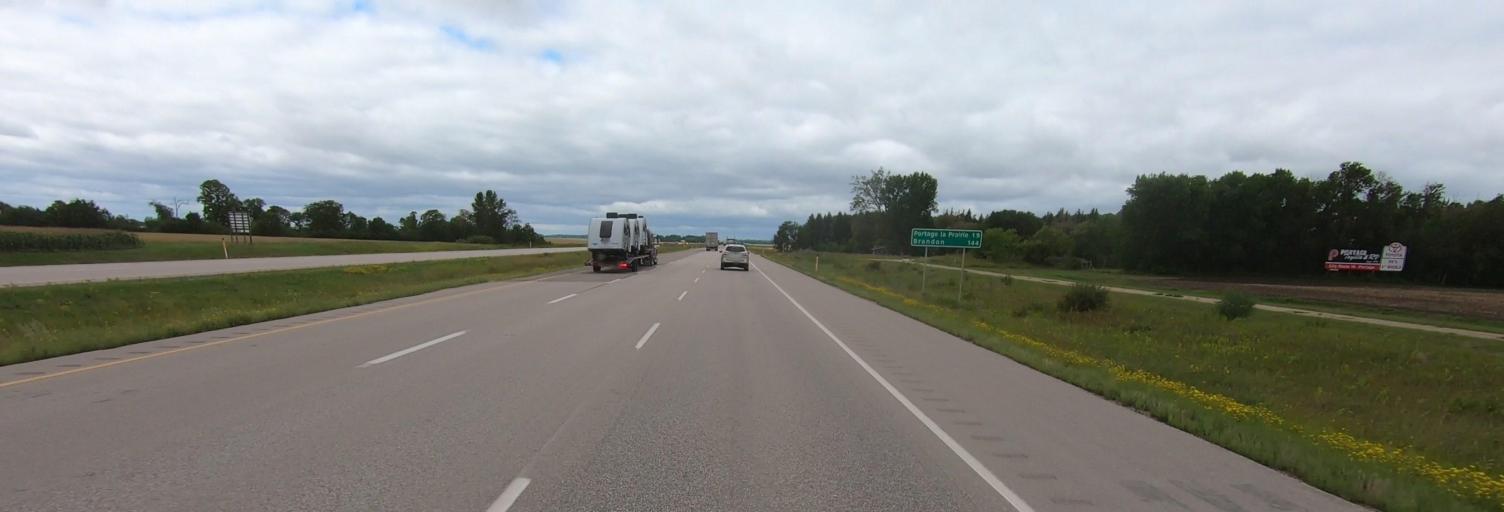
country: CA
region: Manitoba
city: Portage la Prairie
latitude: 49.9555
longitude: -98.0197
